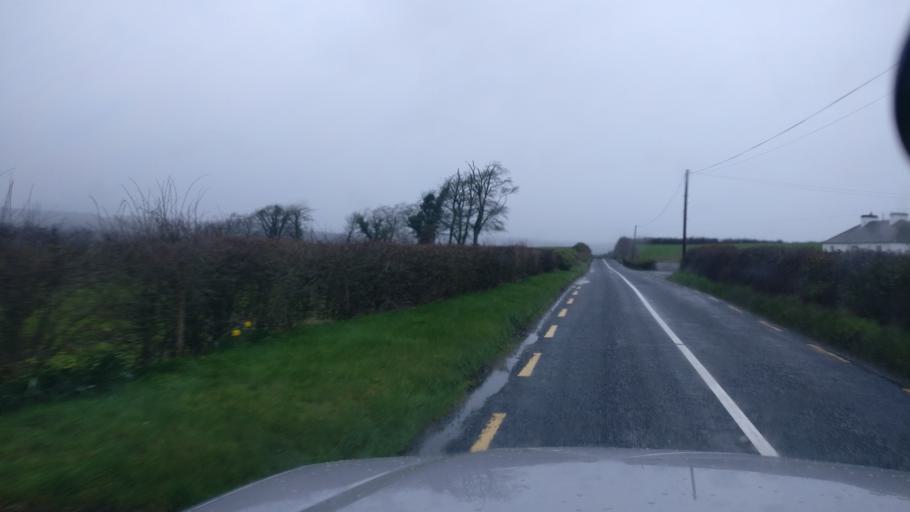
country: IE
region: Connaught
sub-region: County Galway
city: Loughrea
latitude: 53.1175
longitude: -8.4434
